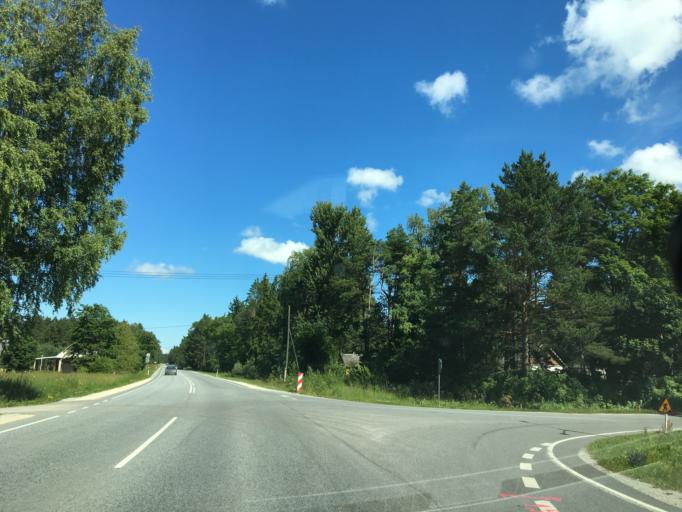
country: EE
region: Harju
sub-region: Nissi vald
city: Riisipere
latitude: 59.2390
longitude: 24.2755
